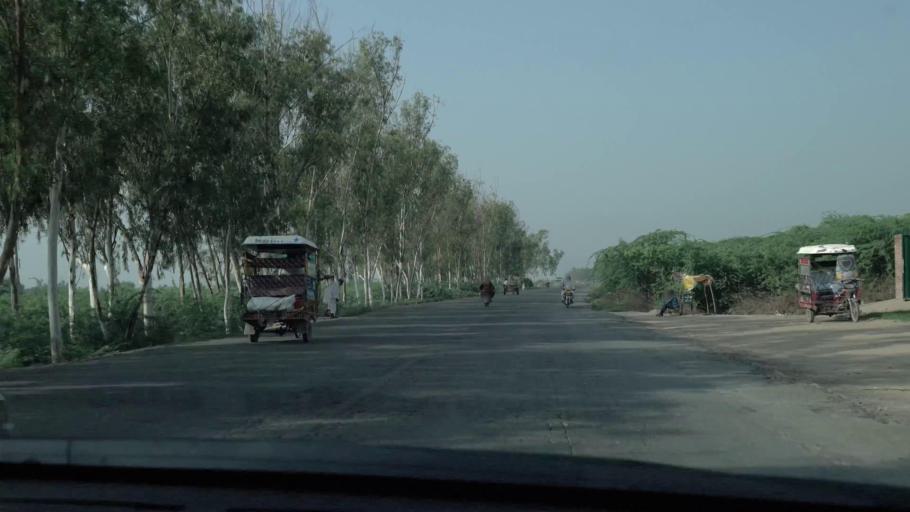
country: PK
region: Punjab
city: Gojra
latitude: 31.1122
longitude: 72.6634
